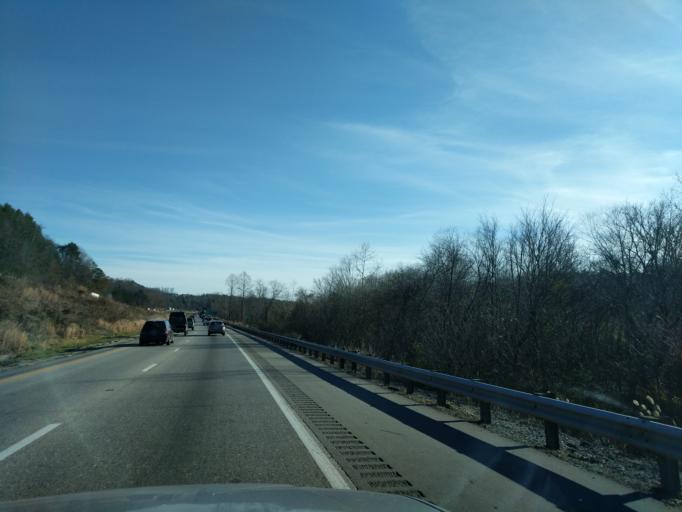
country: US
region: North Carolina
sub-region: Buncombe County
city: Avery Creek
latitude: 35.4672
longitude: -82.5499
